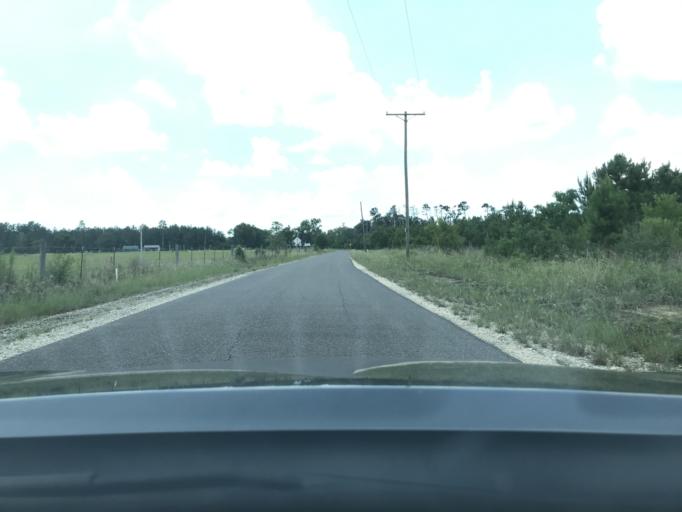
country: US
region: Louisiana
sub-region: Calcasieu Parish
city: Moss Bluff
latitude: 30.3357
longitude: -93.1282
